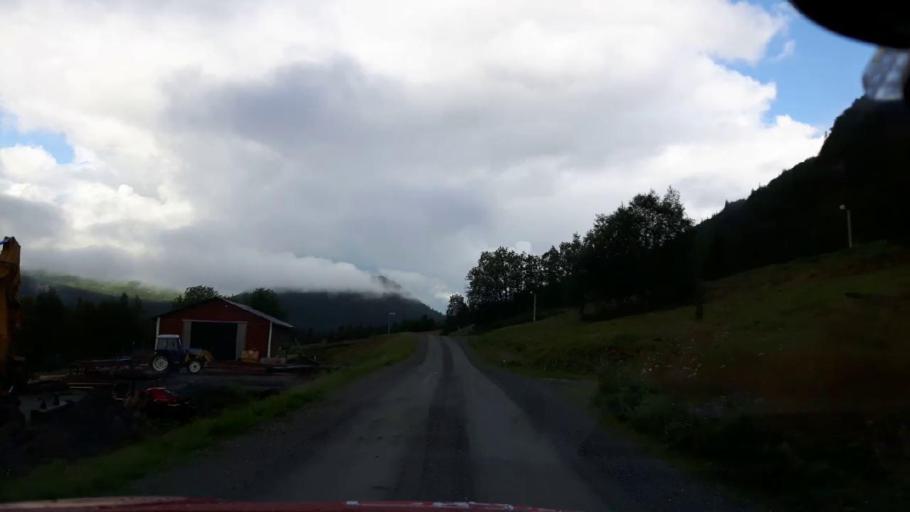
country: NO
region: Nordland
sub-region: Hattfjelldal
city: Hattfjelldal
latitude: 64.8830
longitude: 14.7999
